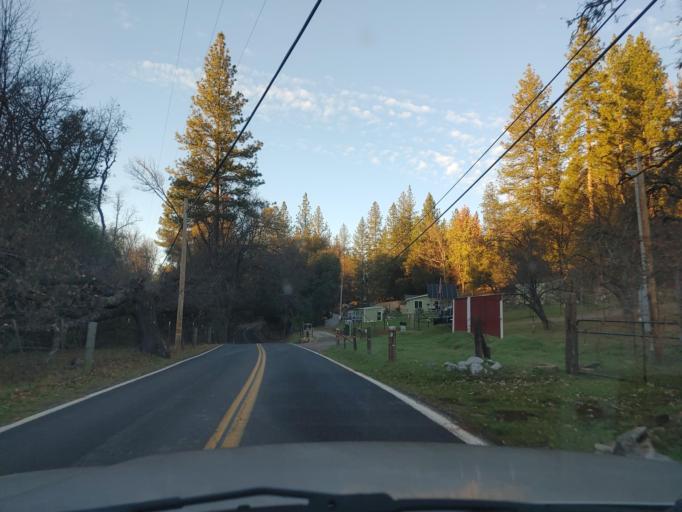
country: US
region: California
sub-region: Tuolumne County
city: Columbia
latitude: 38.0313
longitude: -120.3784
